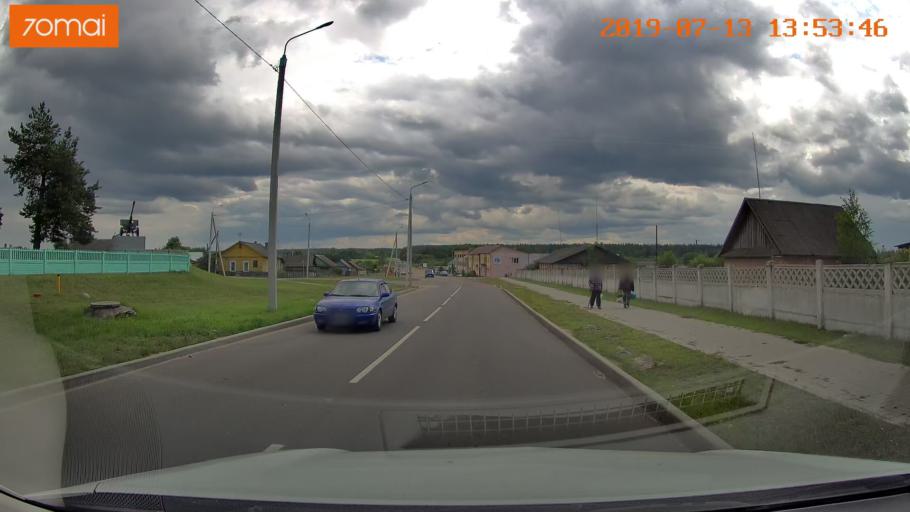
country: BY
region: Mogilev
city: Asipovichy
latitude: 53.2903
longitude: 28.6513
